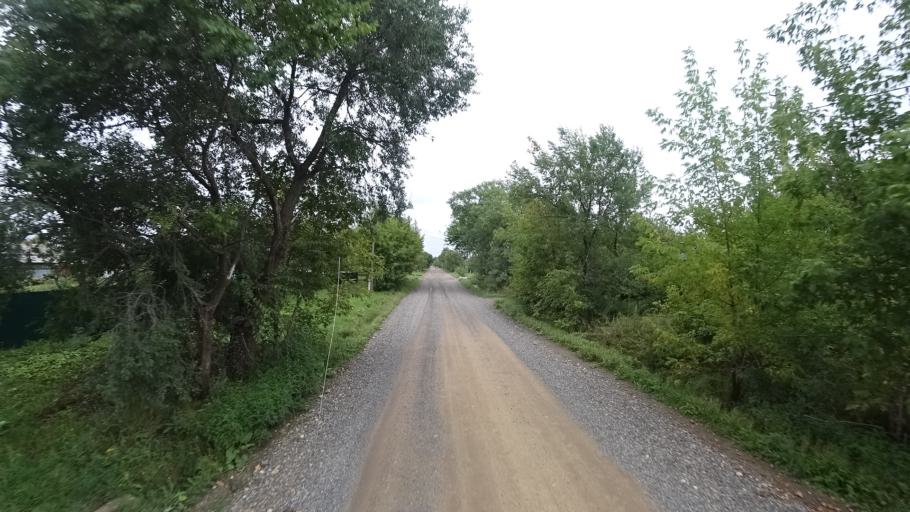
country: RU
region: Primorskiy
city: Chernigovka
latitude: 44.3412
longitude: 132.5642
